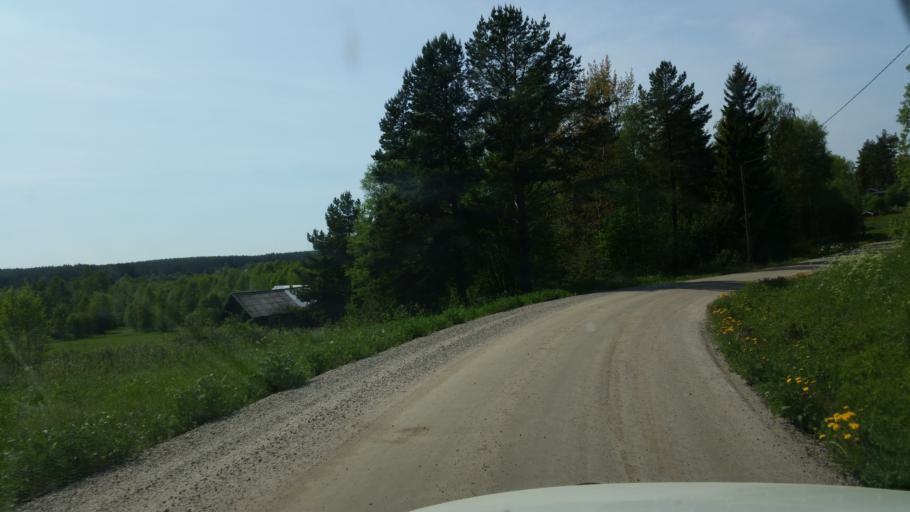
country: SE
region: Gaevleborg
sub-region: Hudiksvalls Kommun
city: Hudiksvall
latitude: 61.8106
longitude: 17.1458
